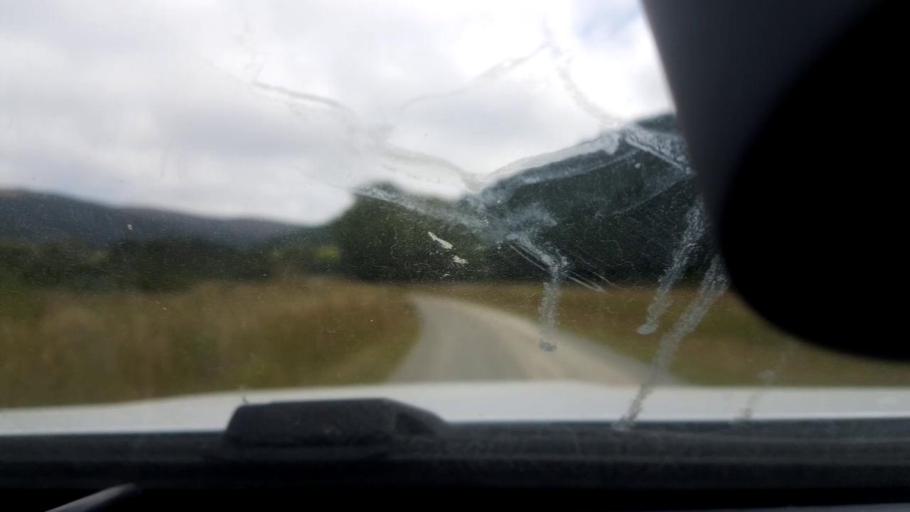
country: NZ
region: Canterbury
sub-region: Timaru District
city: Pleasant Point
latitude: -44.1459
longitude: 171.0889
